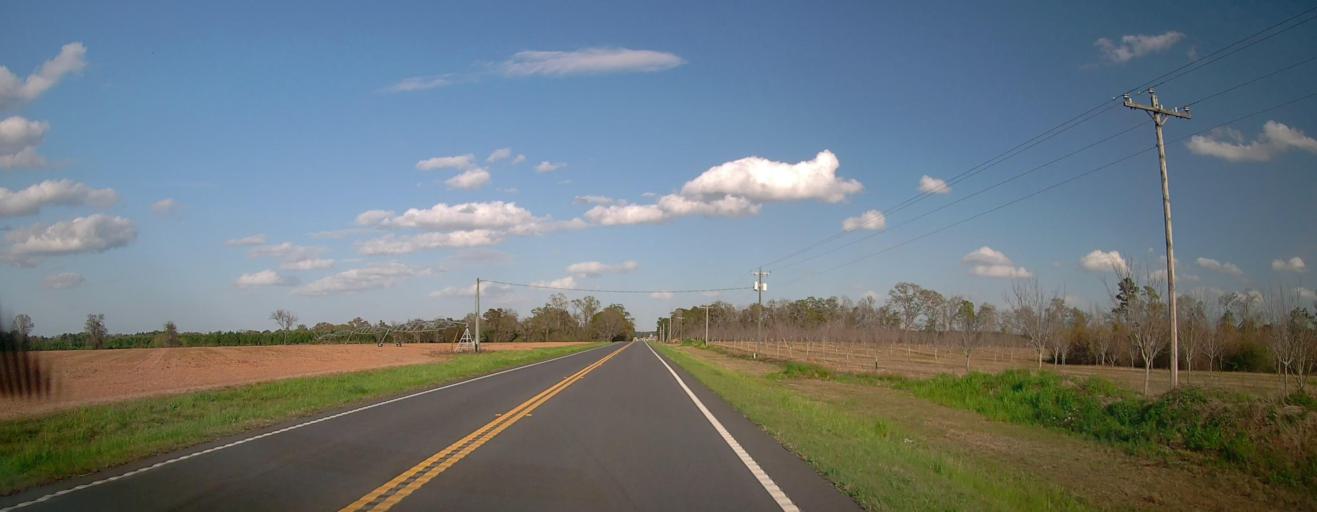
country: US
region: Georgia
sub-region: Toombs County
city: Vidalia
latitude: 32.2074
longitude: -82.4753
